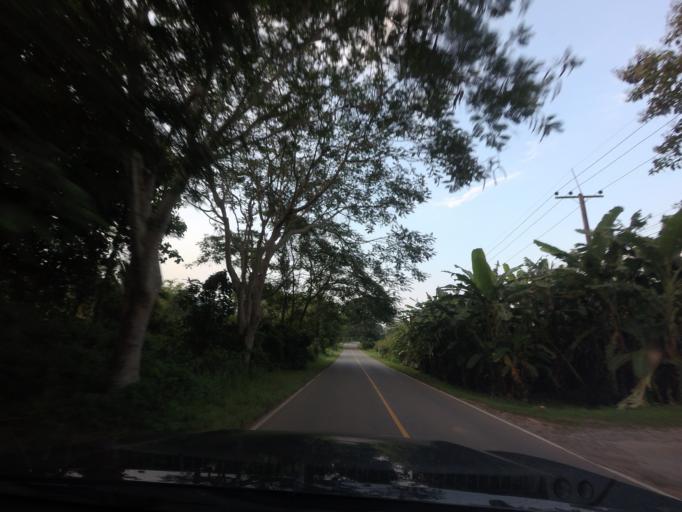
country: TH
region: Loei
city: Na Haeo
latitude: 17.4319
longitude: 101.0511
